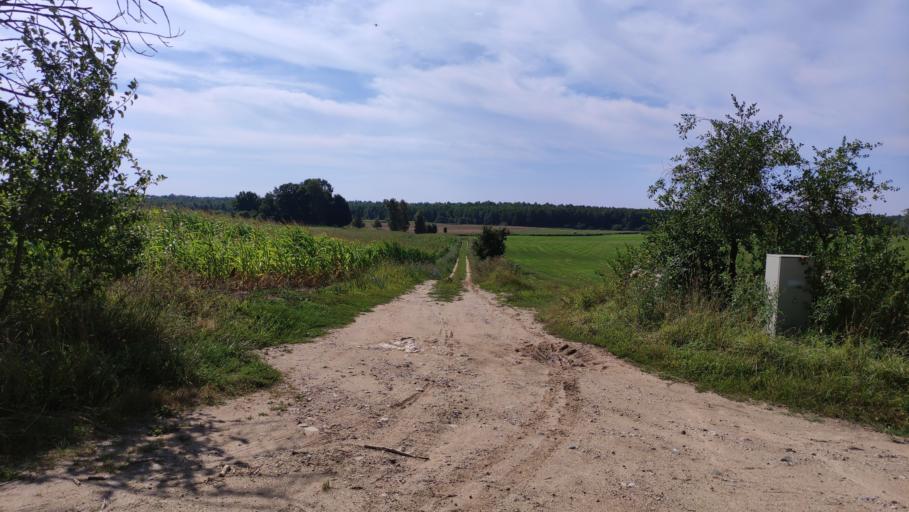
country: LT
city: Simnas
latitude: 54.5167
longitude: 23.6337
